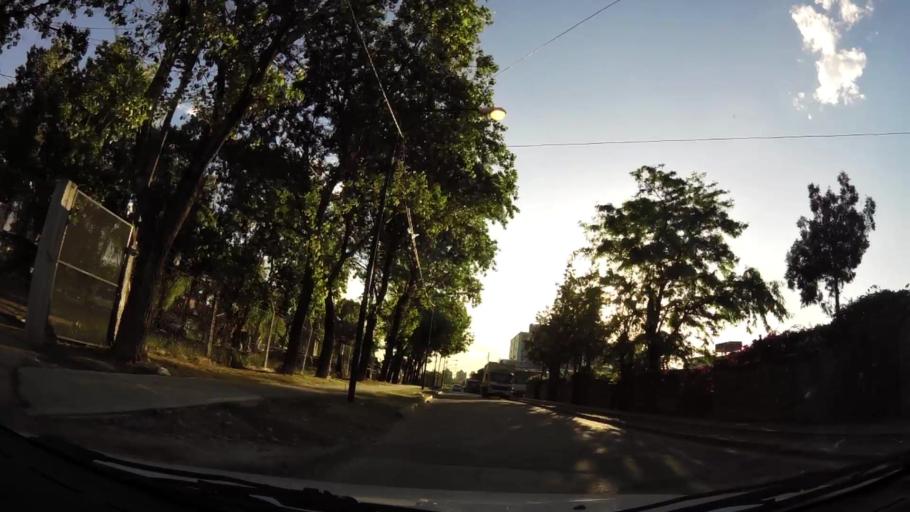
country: AR
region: Buenos Aires
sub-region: Partido de San Isidro
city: San Isidro
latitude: -34.4638
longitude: -58.5475
